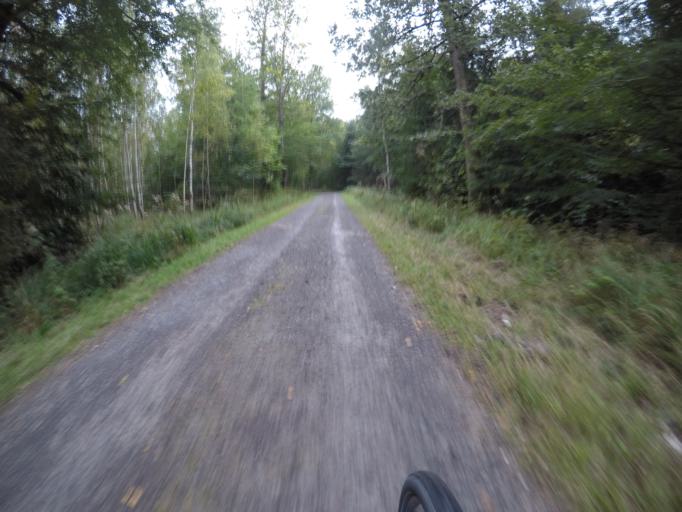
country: DE
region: Baden-Wuerttemberg
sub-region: Regierungsbezirk Stuttgart
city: Gerlingen
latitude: 48.7522
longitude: 9.0553
